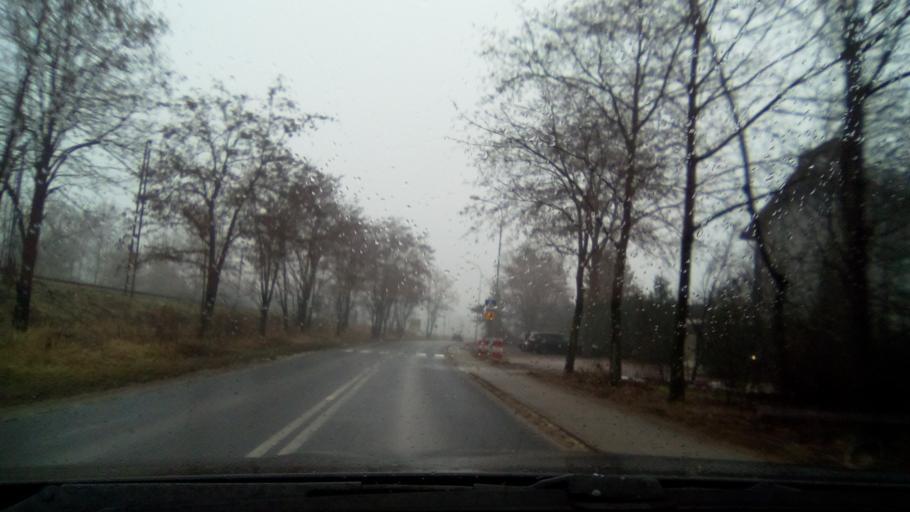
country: PL
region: Greater Poland Voivodeship
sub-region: Powiat poznanski
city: Swarzedz
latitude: 52.4010
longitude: 17.0514
